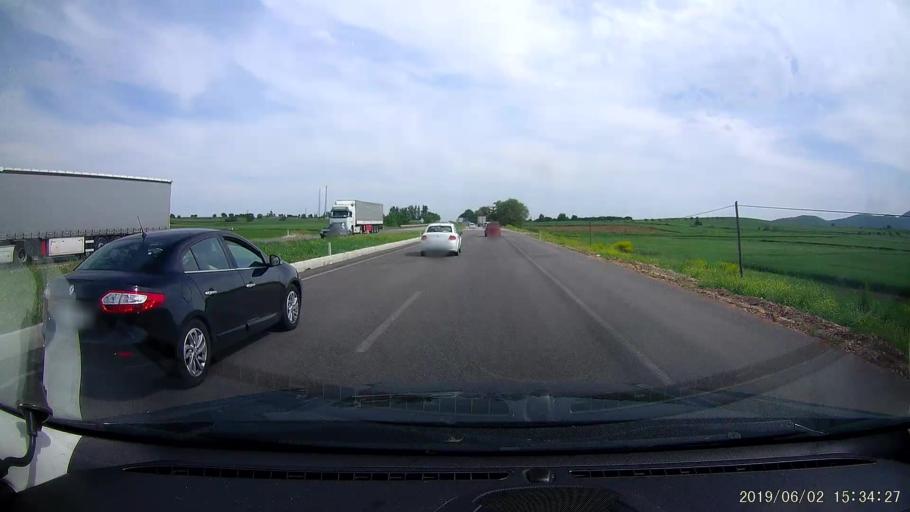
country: TR
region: Amasya
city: Saraycik
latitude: 40.9113
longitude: 35.1739
